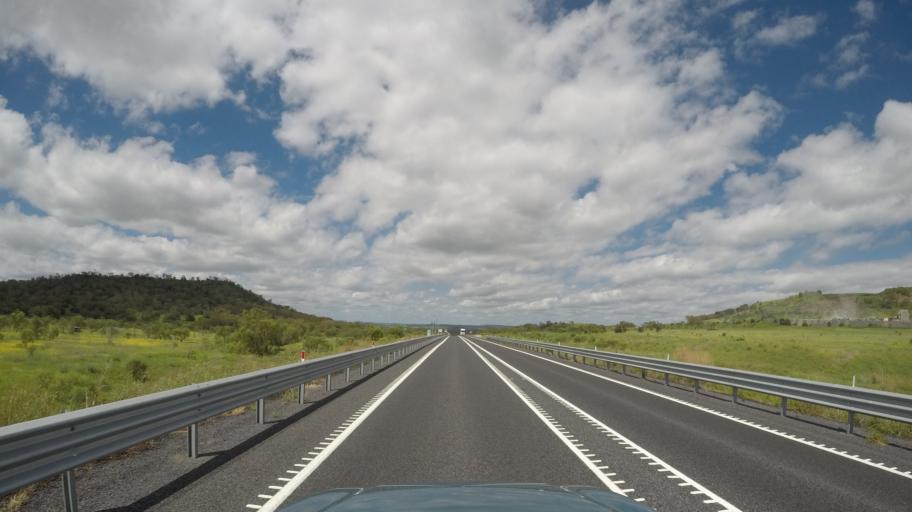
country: AU
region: Queensland
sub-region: Toowoomba
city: Westbrook
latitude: -27.5546
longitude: 151.8244
